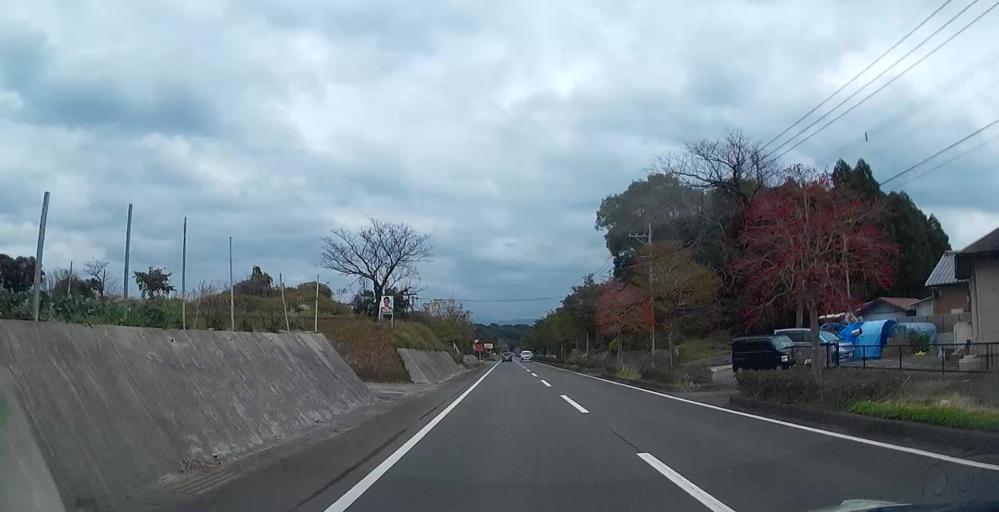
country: JP
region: Kagoshima
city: Akune
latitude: 32.0737
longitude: 130.2133
